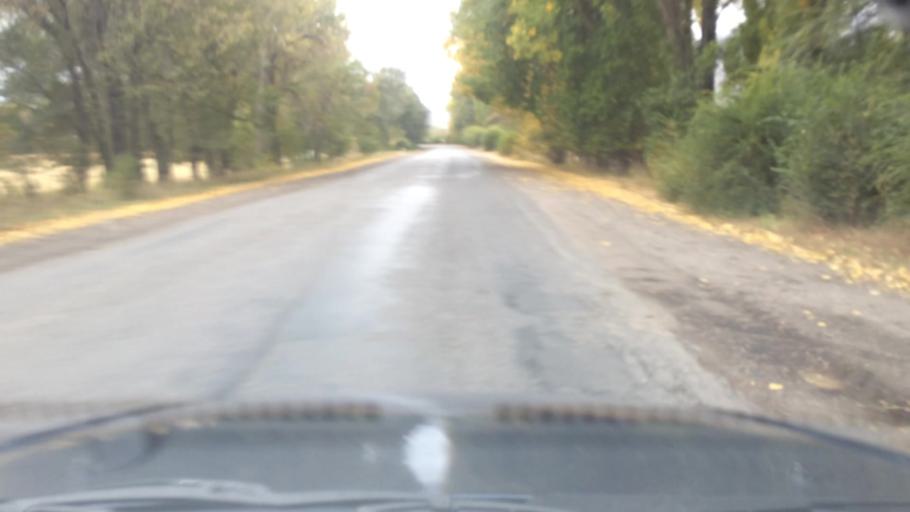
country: KG
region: Ysyk-Koel
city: Tyup
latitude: 42.7812
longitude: 78.2235
